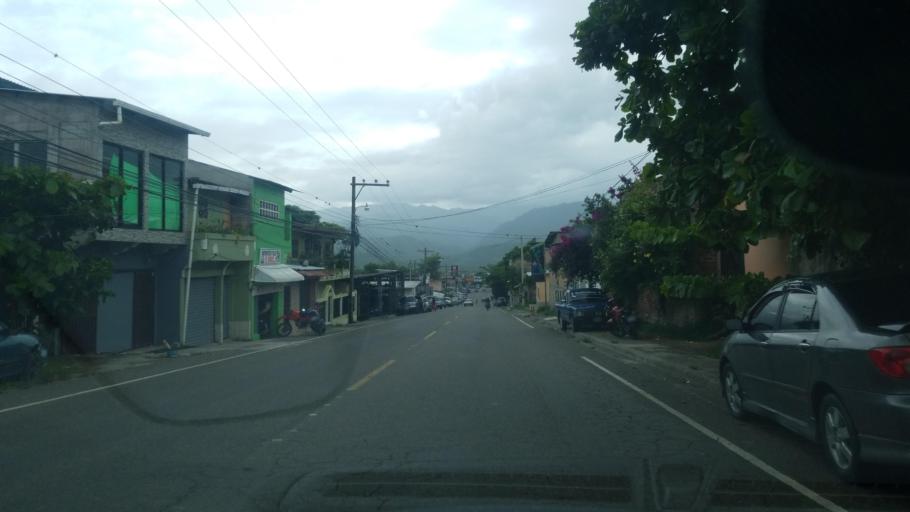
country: HN
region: Ocotepeque
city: Sinuapa
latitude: 14.4425
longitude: -89.1793
